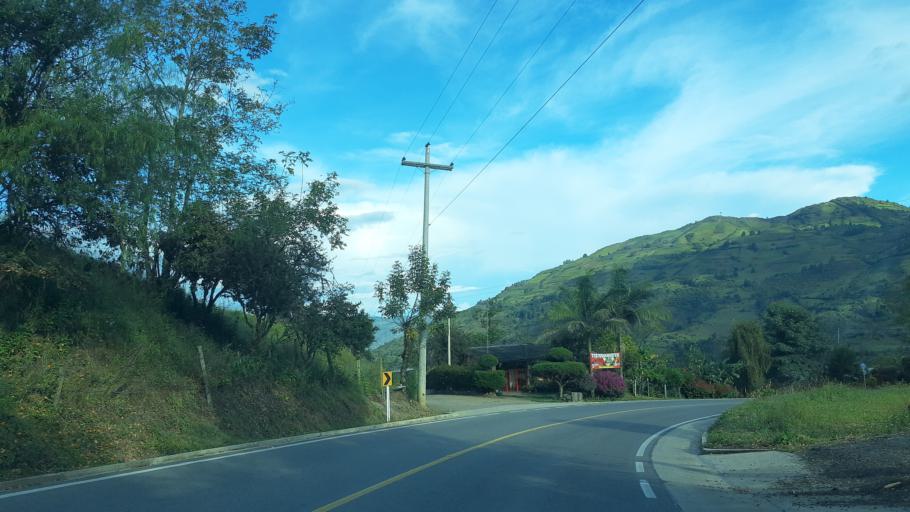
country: CO
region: Cundinamarca
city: Macheta
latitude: 5.0788
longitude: -73.5953
